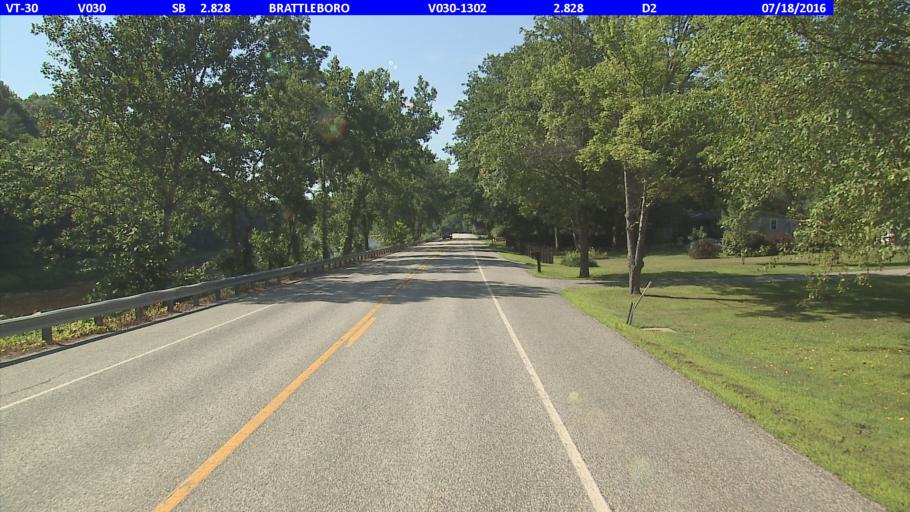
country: US
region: Vermont
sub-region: Windham County
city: West Brattleboro
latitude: 42.8895
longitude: -72.5898
